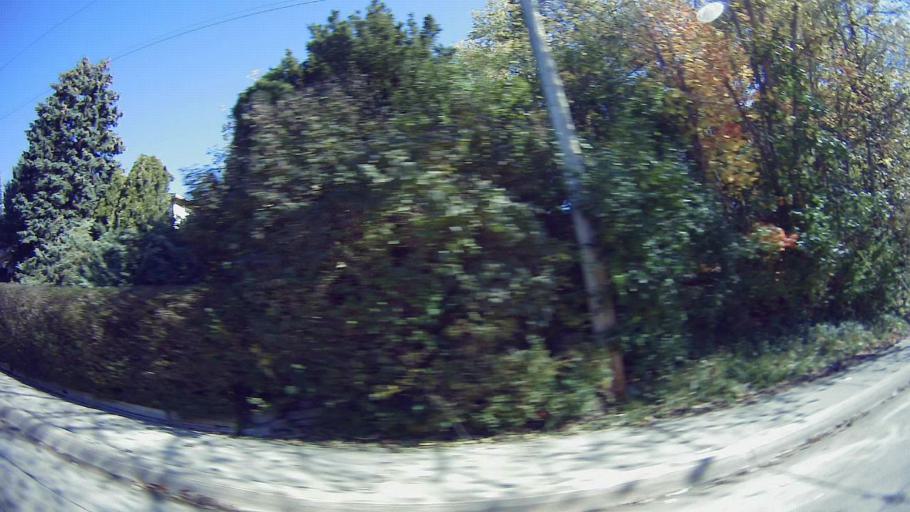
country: US
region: Michigan
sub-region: Oakland County
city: Farmington
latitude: 42.4686
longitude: -83.3742
